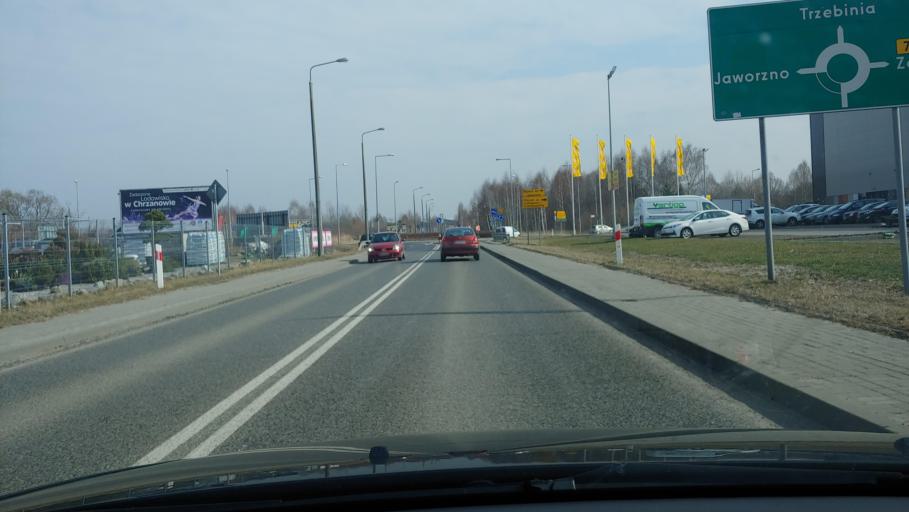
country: PL
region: Lesser Poland Voivodeship
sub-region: Powiat chrzanowski
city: Chrzanow
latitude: 50.1452
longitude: 19.4244
